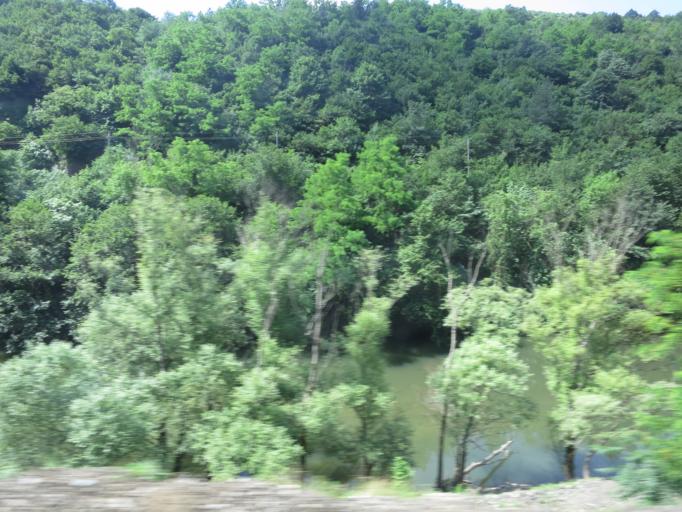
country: GE
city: Shorapani
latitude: 42.0911
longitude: 43.1381
